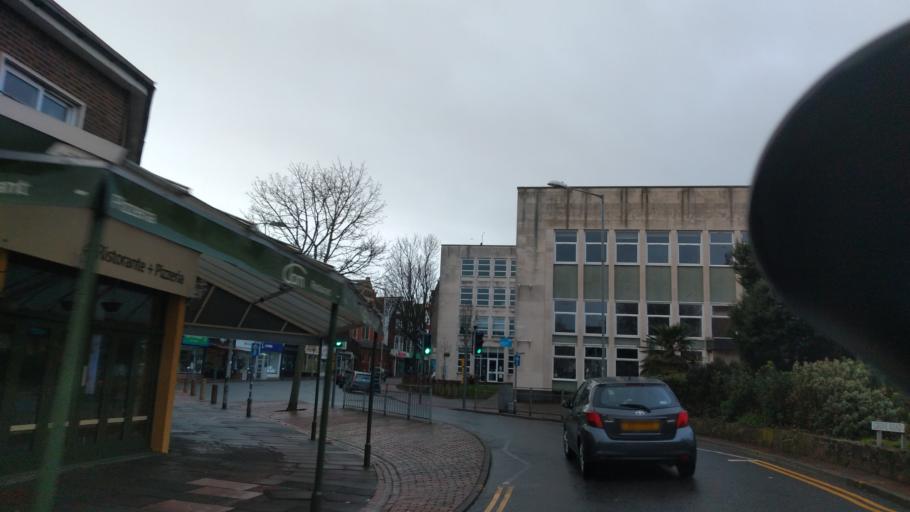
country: GB
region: England
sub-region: East Sussex
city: Eastbourne
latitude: 50.7690
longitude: 0.2798
